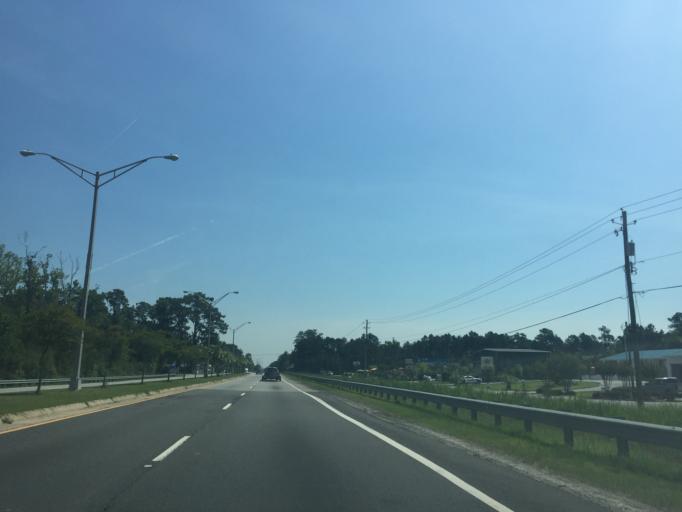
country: US
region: Georgia
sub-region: Bryan County
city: Richmond Hill
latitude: 31.9546
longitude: -81.3085
